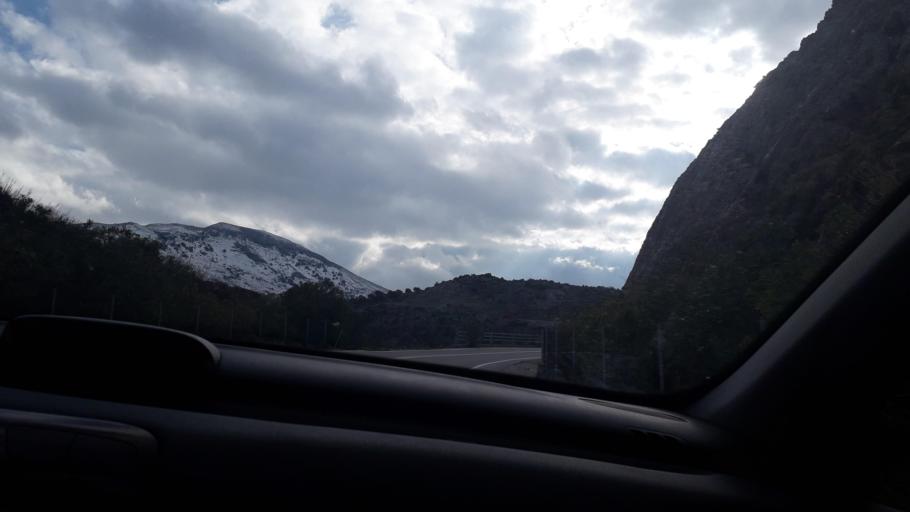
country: GR
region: Crete
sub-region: Nomos Rethymnis
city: Agia Foteini
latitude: 35.2643
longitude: 24.5654
